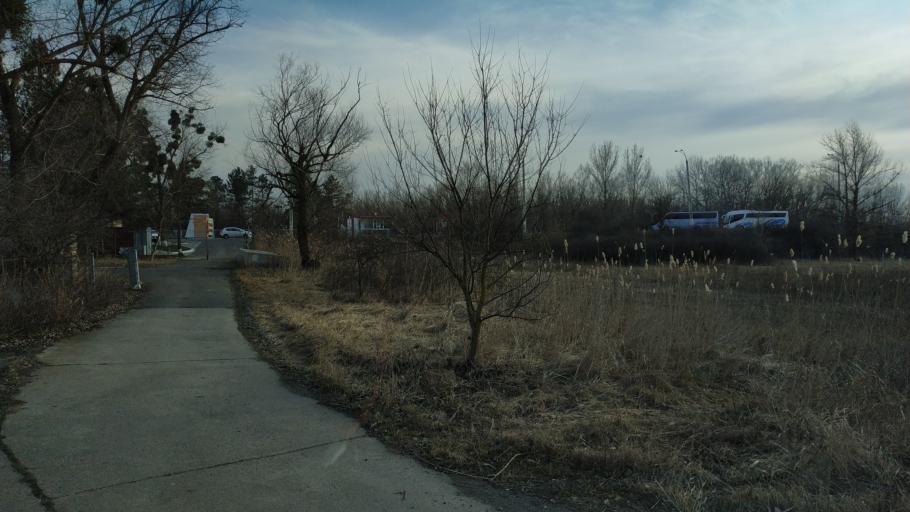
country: RO
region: Vaslui
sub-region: Comuna Dranceni
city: Dranceni
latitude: 46.7946
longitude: 28.1586
